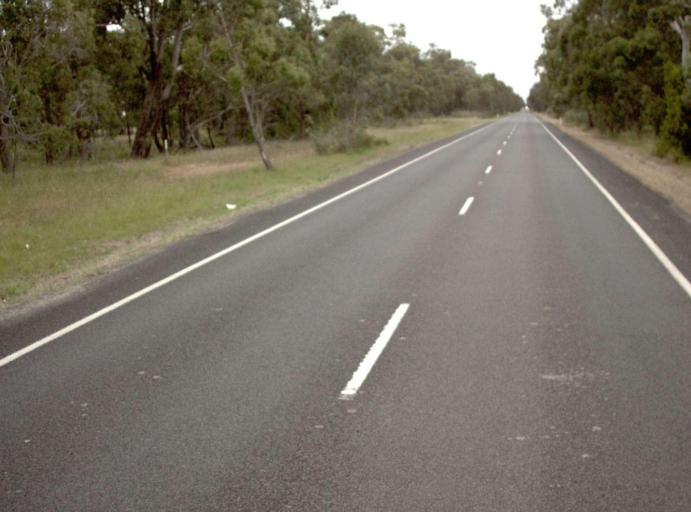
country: AU
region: Victoria
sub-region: Wellington
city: Sale
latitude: -38.3525
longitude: 146.9972
